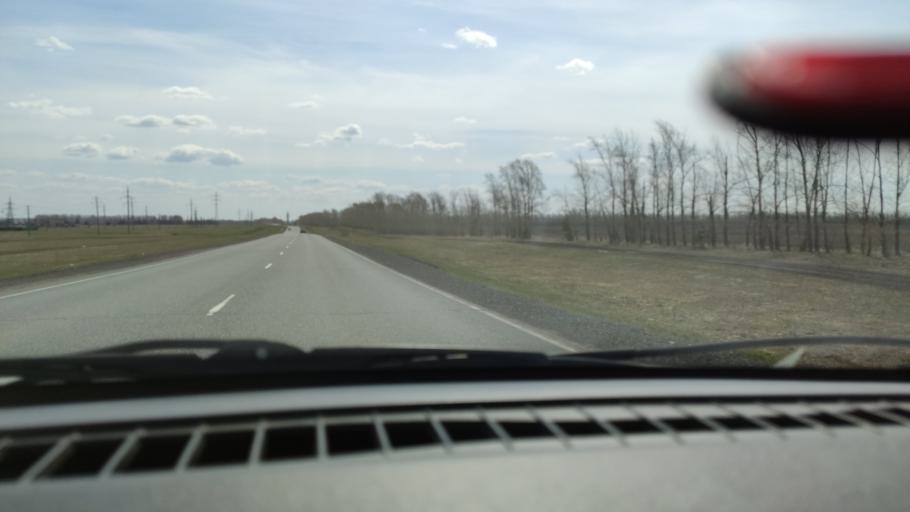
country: RU
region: Bashkortostan
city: Kushnarenkovo
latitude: 55.2038
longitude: 55.1063
